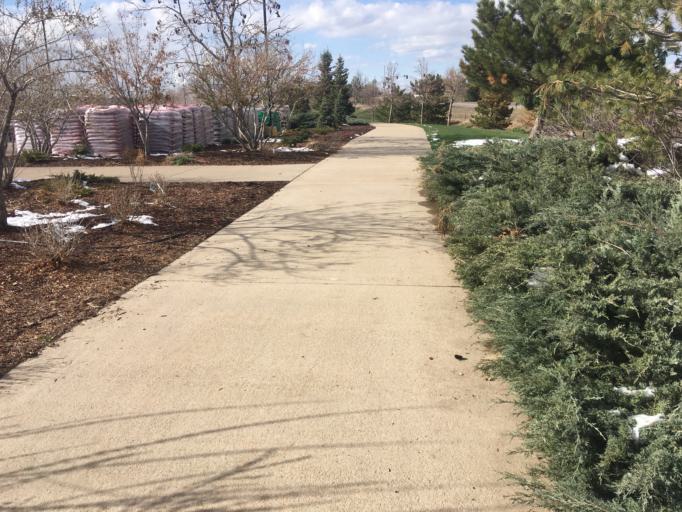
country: US
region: Colorado
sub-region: Adams County
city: Northglenn
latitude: 39.9408
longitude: -104.9891
